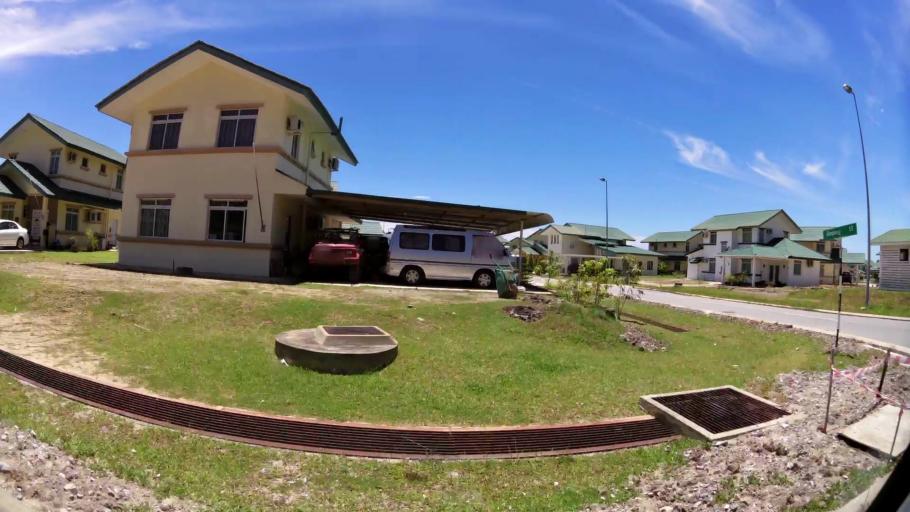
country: BN
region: Brunei and Muara
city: Bandar Seri Begawan
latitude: 5.0218
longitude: 115.0358
